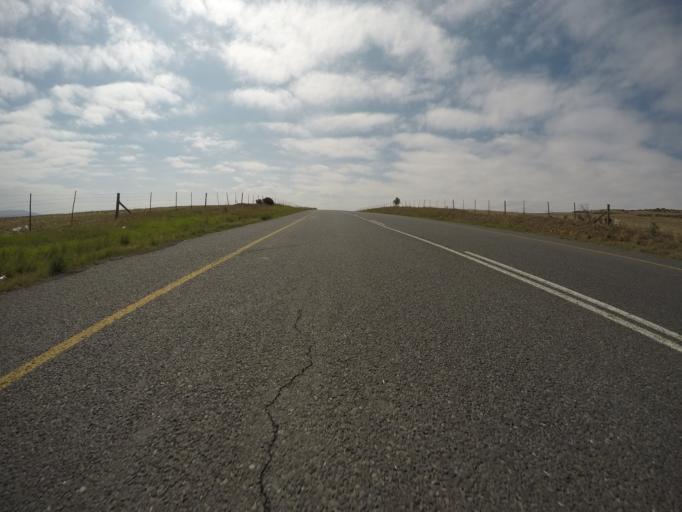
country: ZA
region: Western Cape
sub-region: City of Cape Town
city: Sunset Beach
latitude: -33.7939
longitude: 18.5715
